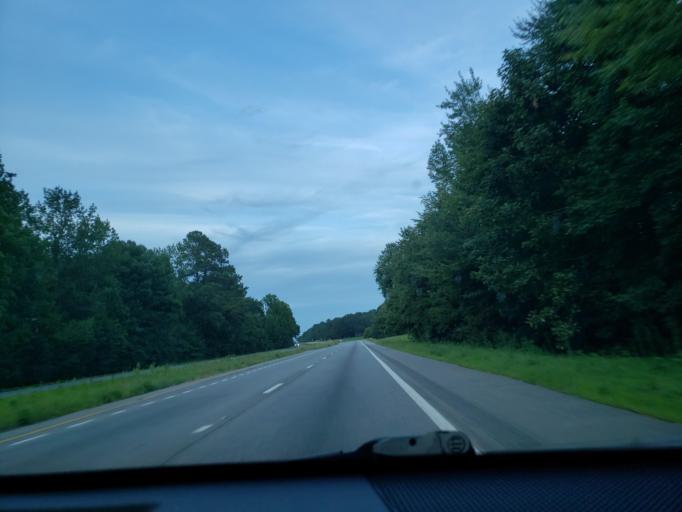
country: US
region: Virginia
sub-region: Southampton County
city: Courtland
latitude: 36.7017
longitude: -77.2406
